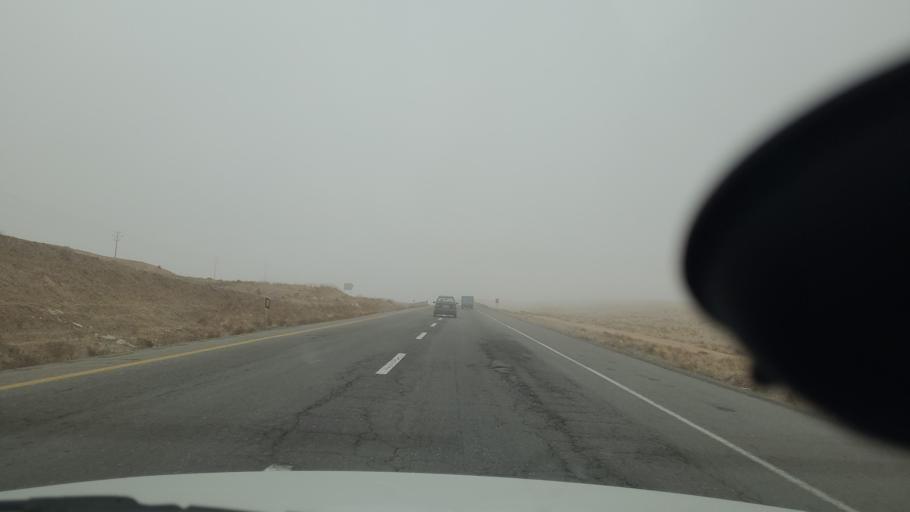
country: IR
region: Razavi Khorasan
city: Fariman
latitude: 35.8034
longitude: 59.7447
